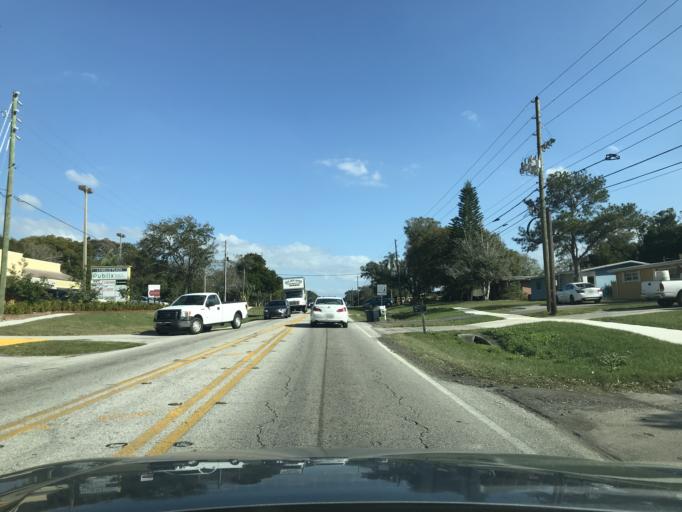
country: US
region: Florida
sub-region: Pinellas County
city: Belleair
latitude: 27.9389
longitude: -82.7744
